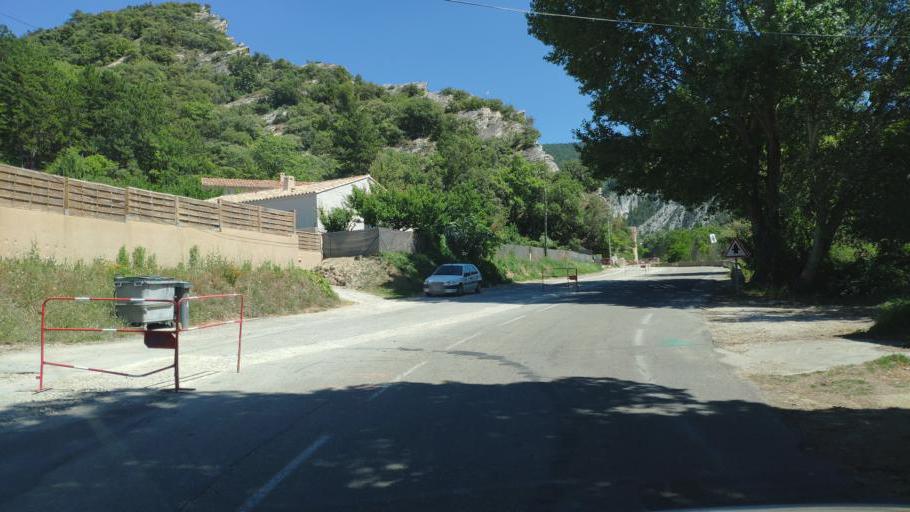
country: FR
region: Provence-Alpes-Cote d'Azur
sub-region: Departement du Vaucluse
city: Malaucene
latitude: 44.1707
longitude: 5.1402
